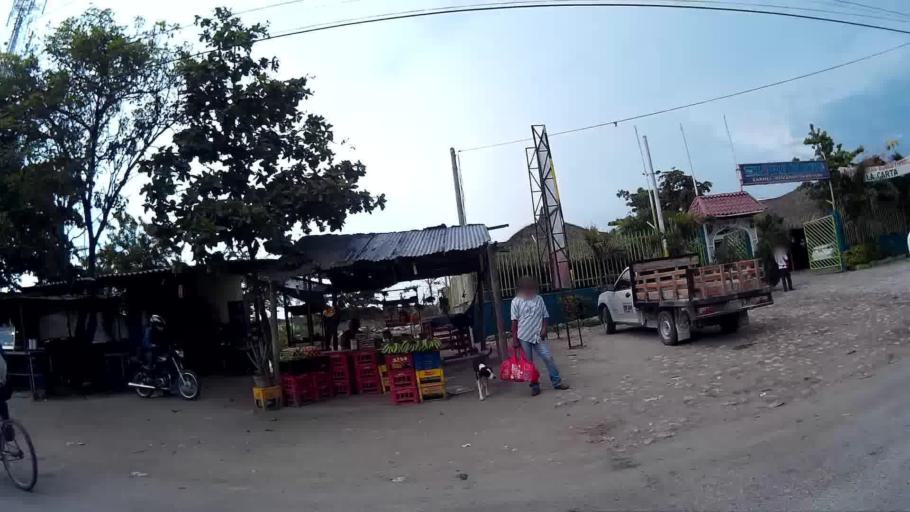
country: CO
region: Magdalena
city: Cienaga
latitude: 11.0042
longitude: -74.2287
